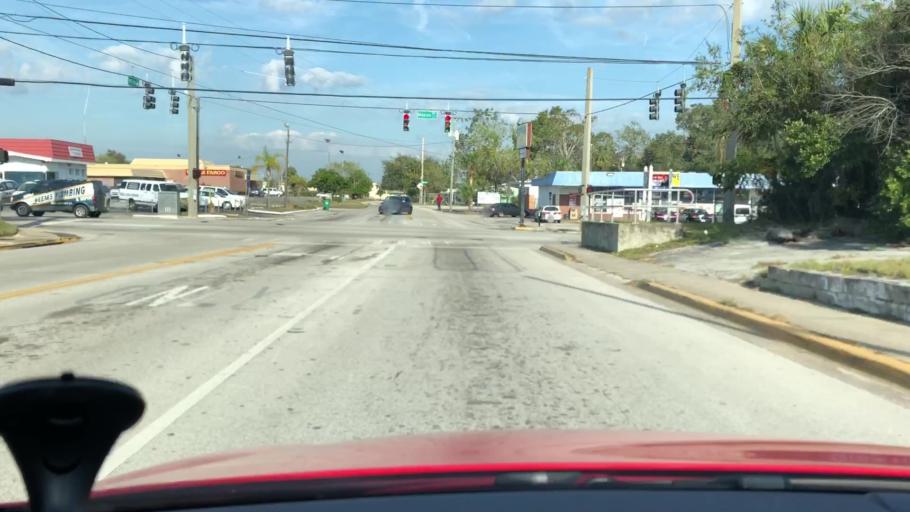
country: US
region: Florida
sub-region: Volusia County
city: Holly Hill
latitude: 29.2167
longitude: -81.0538
